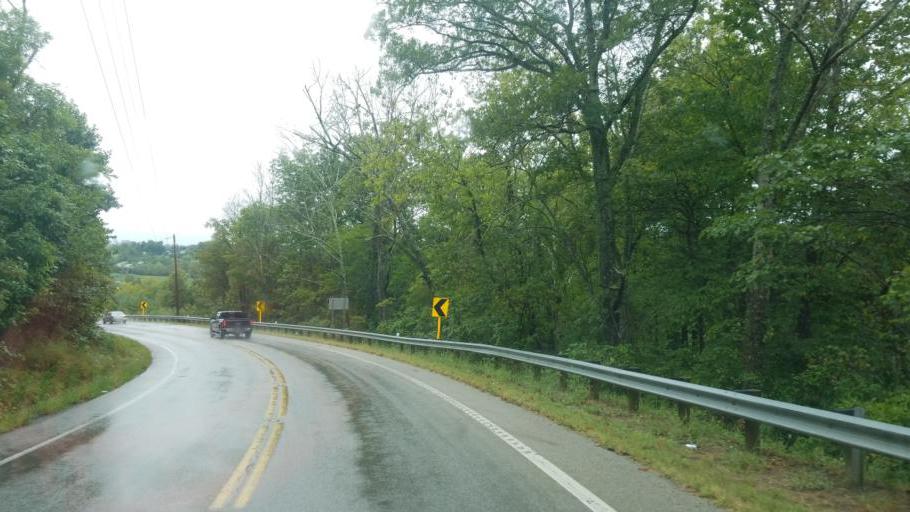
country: US
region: Ohio
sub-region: Adams County
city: West Union
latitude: 38.7988
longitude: -83.5051
